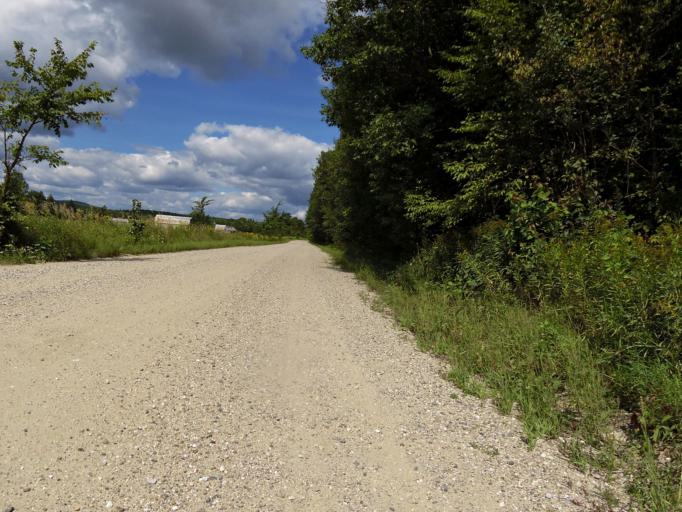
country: CA
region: Quebec
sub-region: Outaouais
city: Wakefield
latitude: 45.8046
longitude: -76.0291
